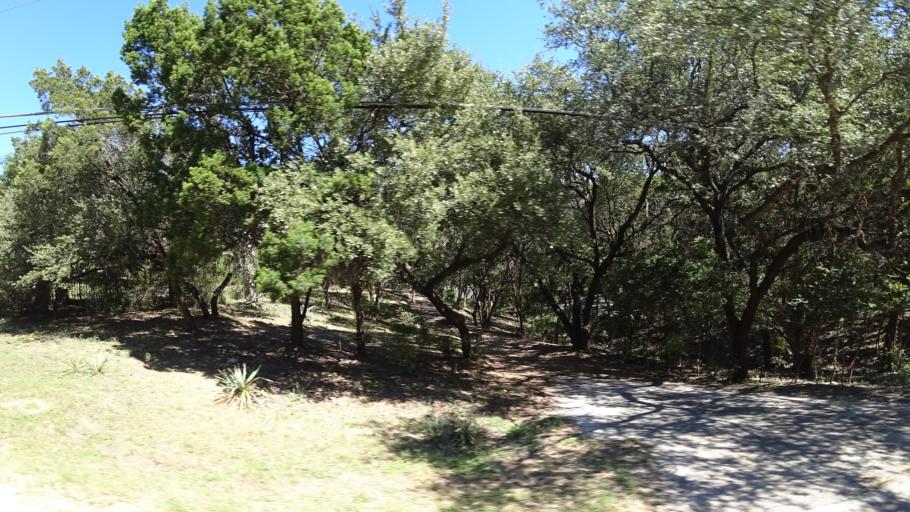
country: US
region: Texas
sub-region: Travis County
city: West Lake Hills
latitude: 30.3265
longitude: -97.7806
